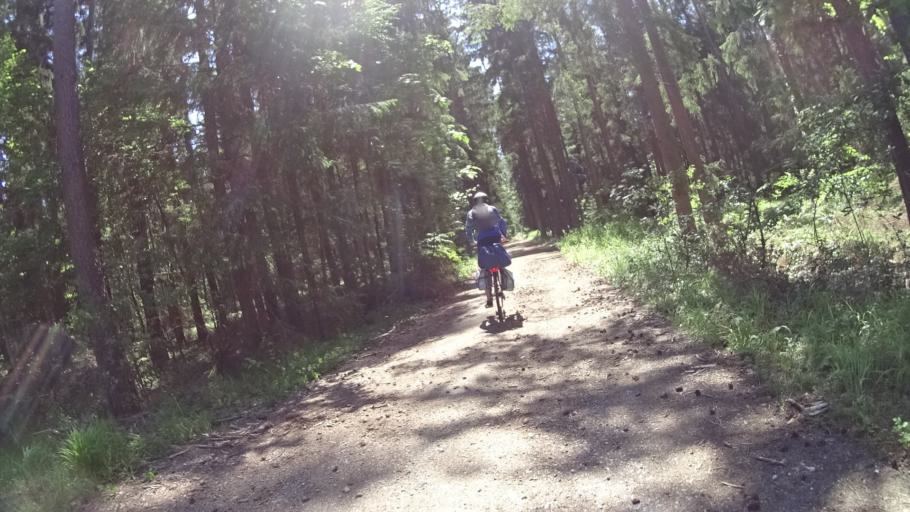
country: DE
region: Bavaria
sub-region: Regierungsbezirk Mittelfranken
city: Pfofeld
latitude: 49.1239
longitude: 10.8360
